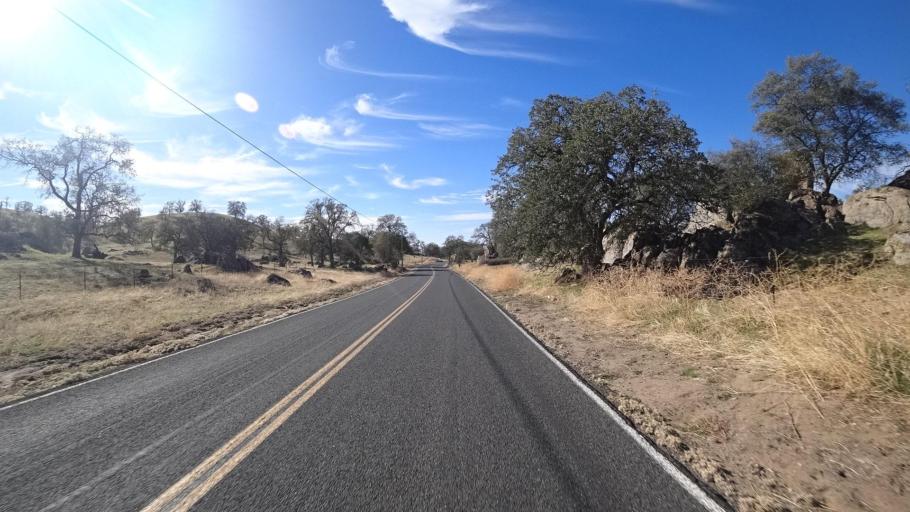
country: US
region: California
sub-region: Kern County
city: Oildale
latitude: 35.6270
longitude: -118.8391
